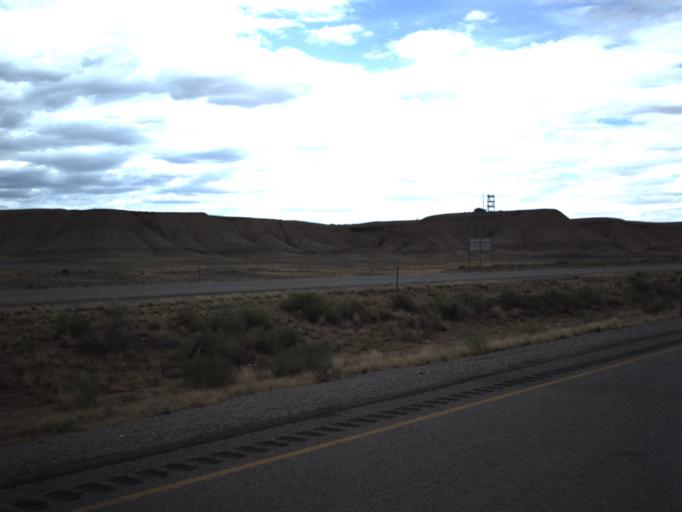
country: US
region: Utah
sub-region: Carbon County
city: East Carbon City
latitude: 38.9743
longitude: -110.1104
